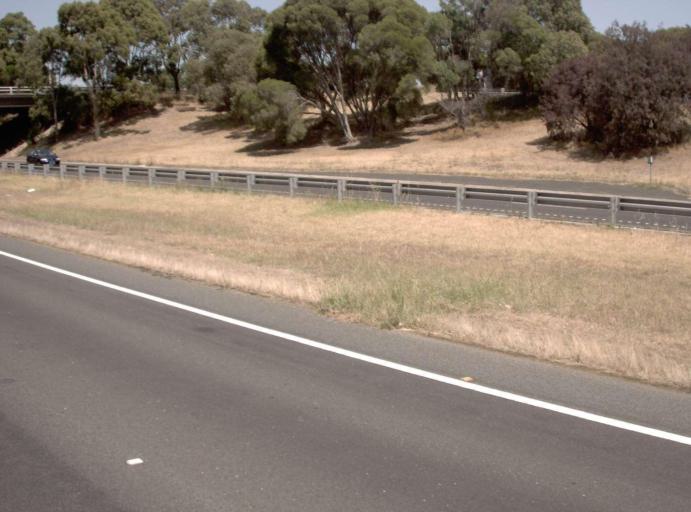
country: AU
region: Victoria
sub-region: Frankston
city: Seaford
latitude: -38.1079
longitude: 145.1396
